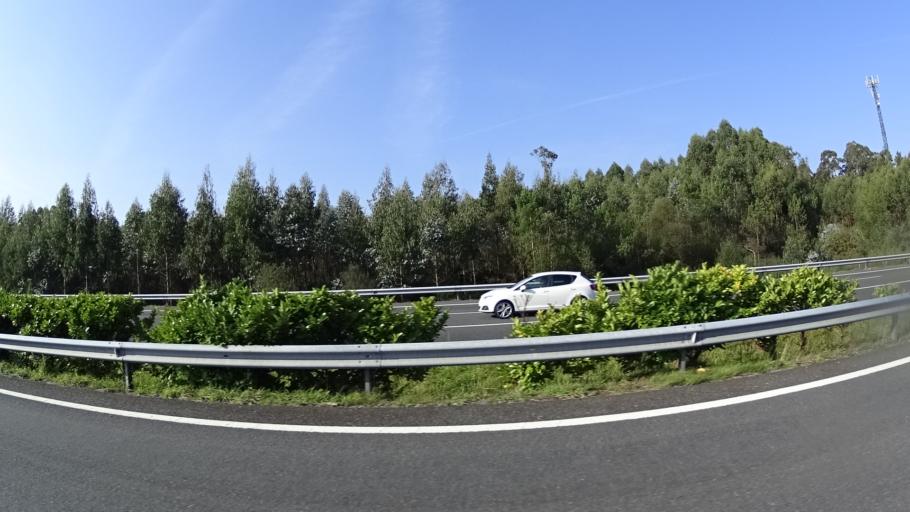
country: ES
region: Galicia
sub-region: Provincia da Coruna
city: Coiros
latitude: 43.2425
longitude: -8.1436
